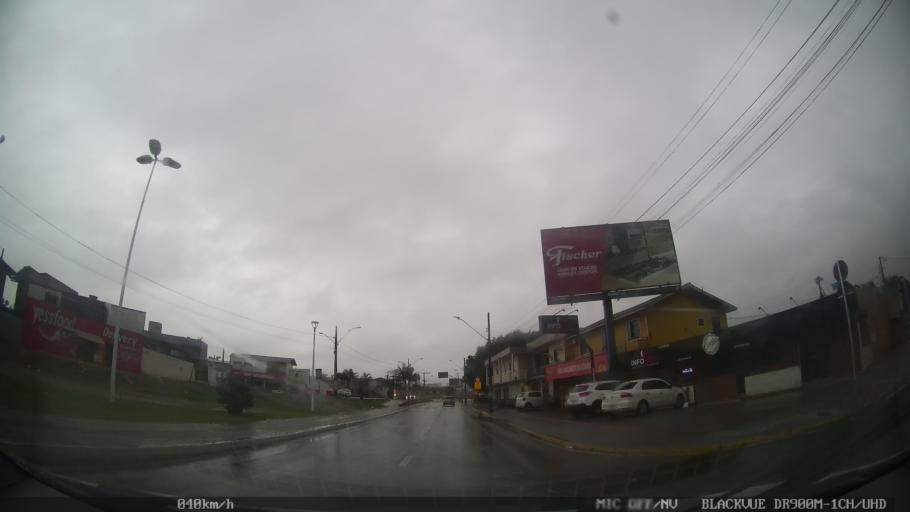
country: BR
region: Santa Catarina
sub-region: Navegantes
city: Navegantes
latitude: -26.8845
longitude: -48.6532
